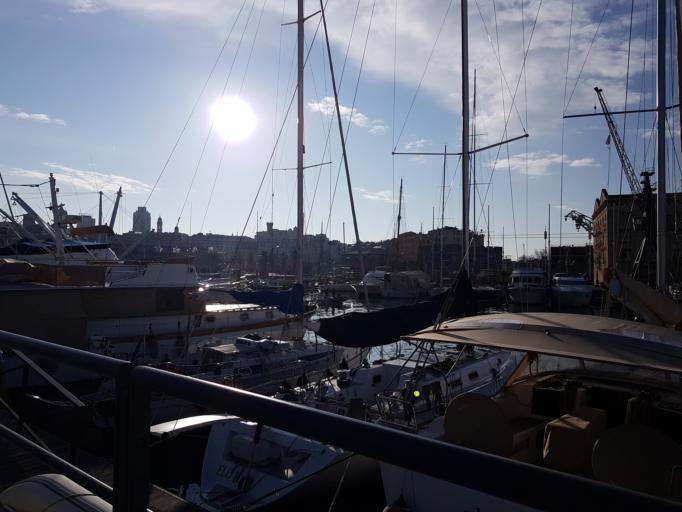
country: IT
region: Liguria
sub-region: Provincia di Genova
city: San Teodoro
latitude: 44.4101
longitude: 8.9233
